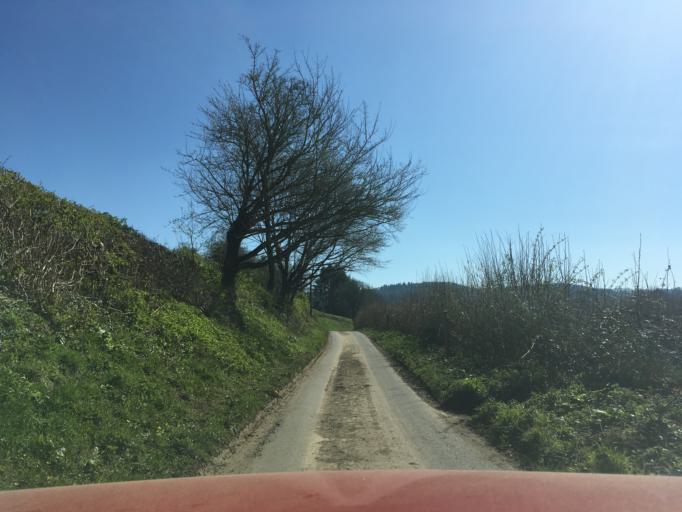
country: GB
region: England
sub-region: Gloucestershire
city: Dursley
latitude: 51.6658
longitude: -2.3575
